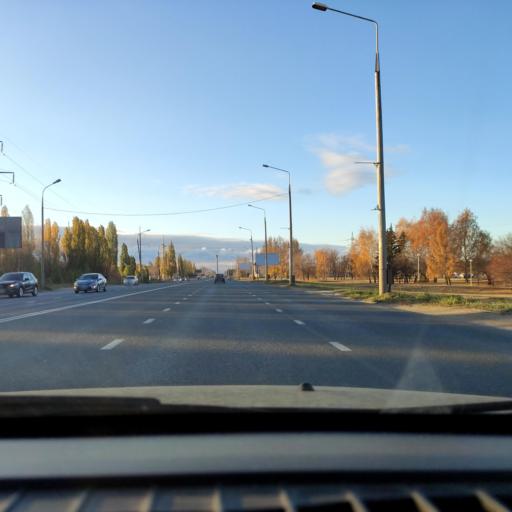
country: RU
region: Samara
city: Tol'yatti
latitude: 53.5600
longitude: 49.2892
